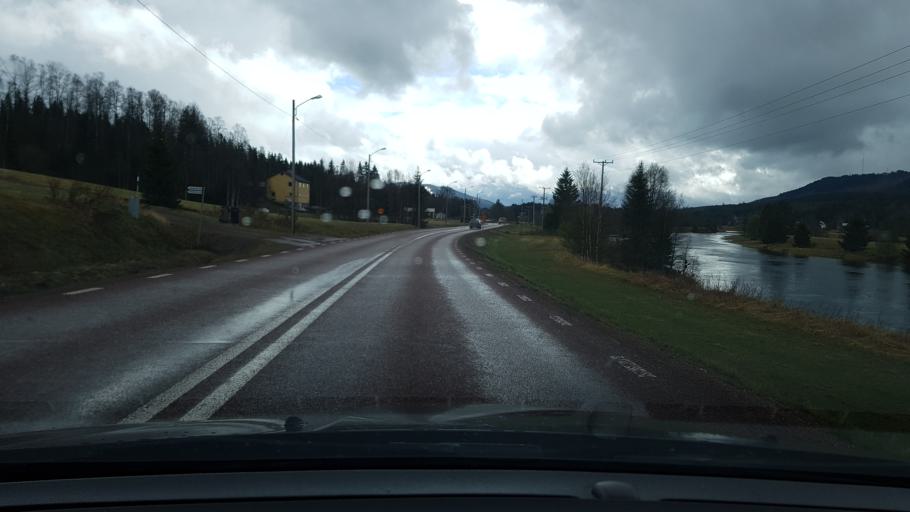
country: SE
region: Dalarna
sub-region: Malung-Saelens kommun
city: Malung
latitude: 61.0865
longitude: 13.3223
